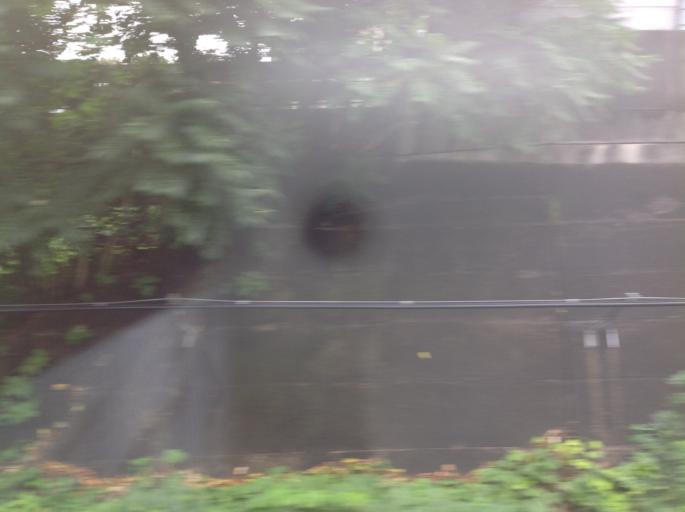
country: JP
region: Iwate
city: Ichinoseki
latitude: 38.9199
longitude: 141.1363
